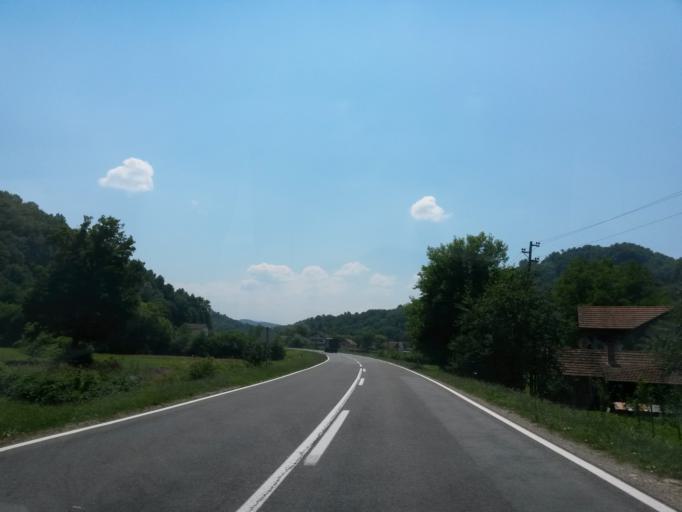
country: BA
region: Federation of Bosnia and Herzegovina
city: Lijesnica
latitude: 44.5145
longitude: 18.0814
